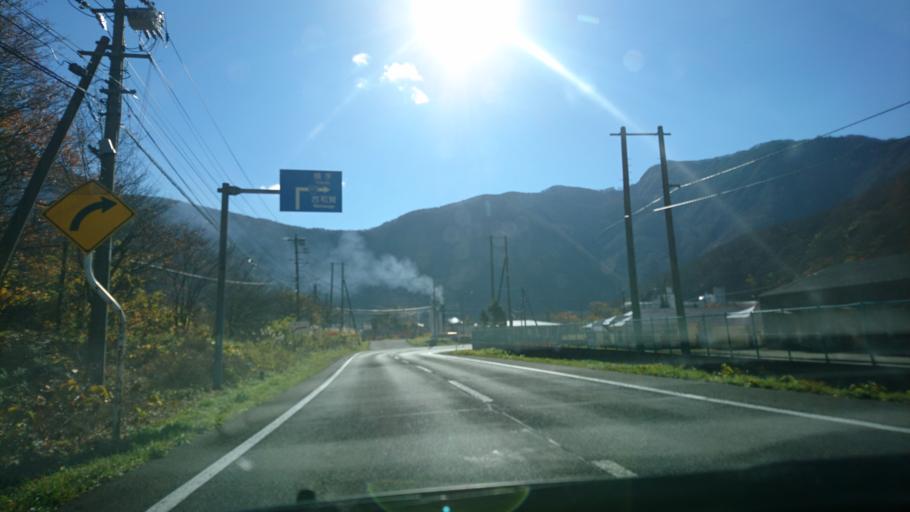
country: JP
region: Iwate
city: Kitakami
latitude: 39.3059
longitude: 140.9021
